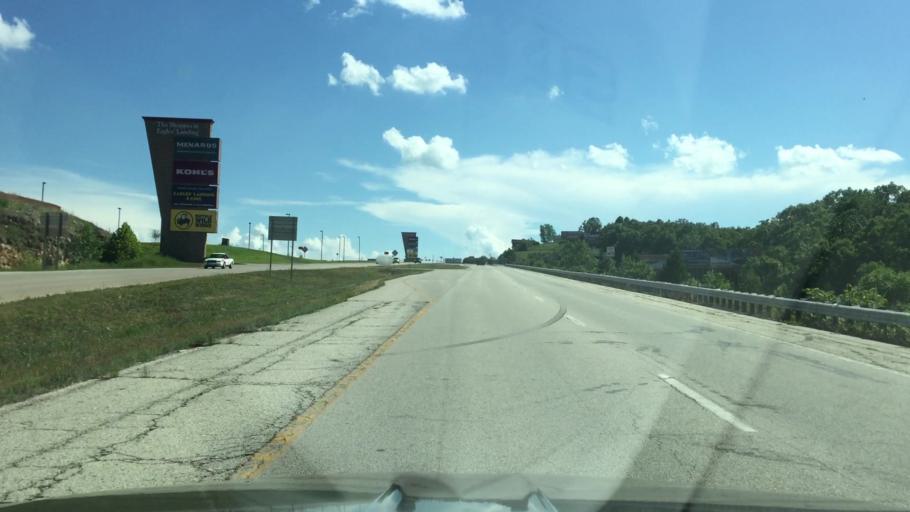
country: US
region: Missouri
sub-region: Miller County
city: Lake Ozark
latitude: 38.1815
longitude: -92.6117
